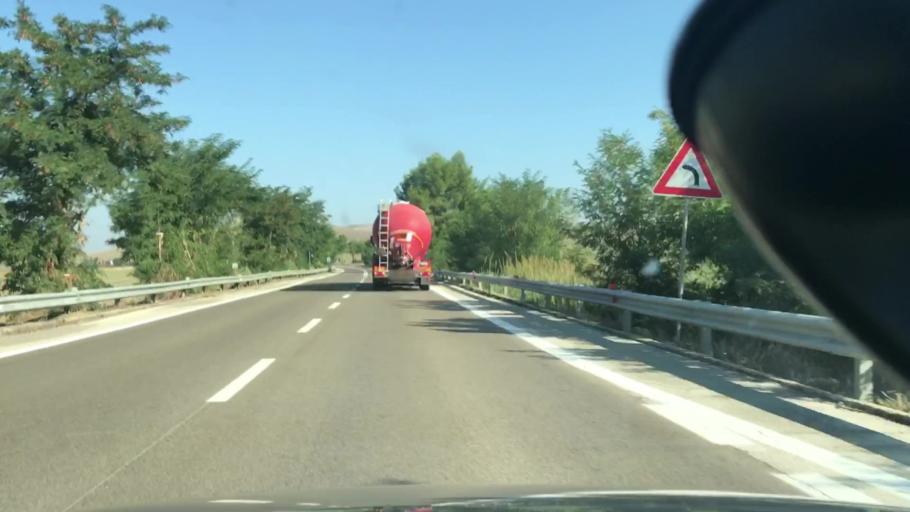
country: IT
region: Basilicate
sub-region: Provincia di Matera
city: Irsina
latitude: 40.8030
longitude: 16.2740
